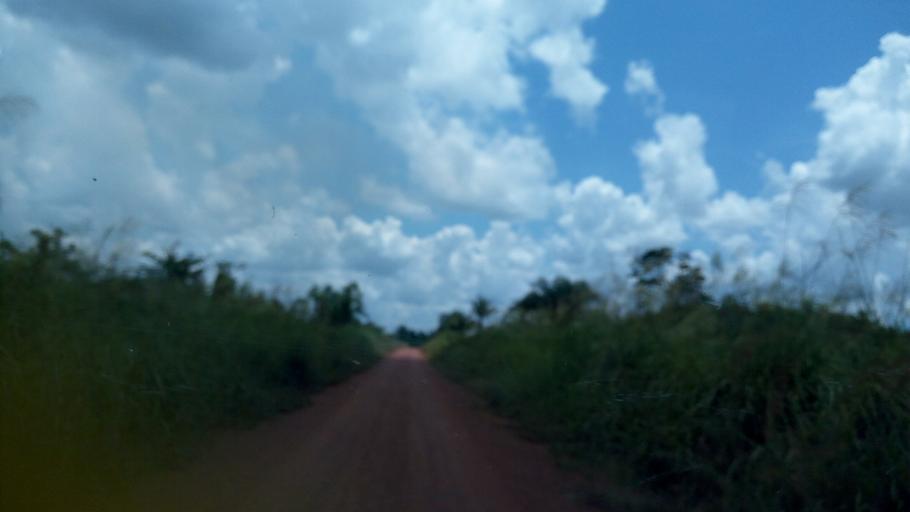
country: CD
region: Equateur
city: Gemena
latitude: 3.5667
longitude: 19.2668
